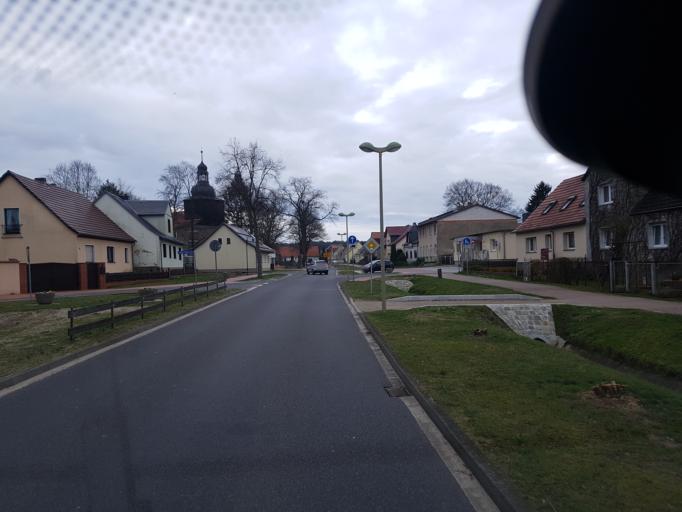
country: DE
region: Brandenburg
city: Gross Lindow
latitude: 52.1444
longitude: 14.5305
